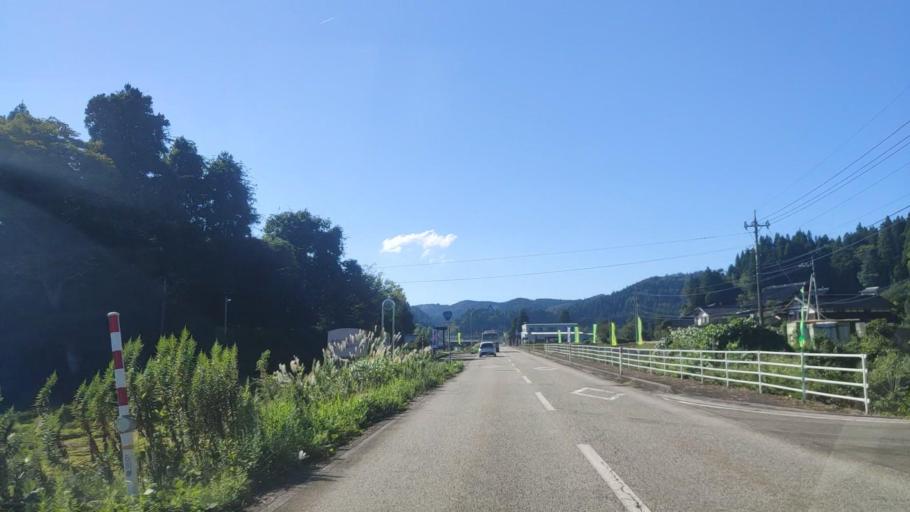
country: JP
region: Ishikawa
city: Nanao
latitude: 37.2793
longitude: 137.0484
